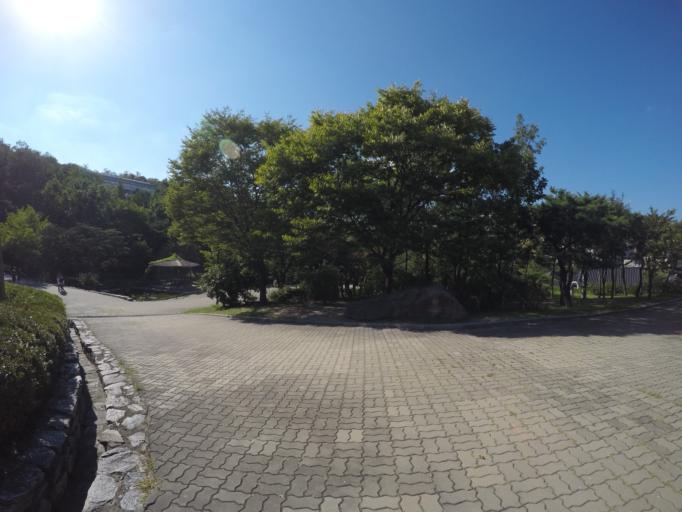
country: KR
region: Seoul
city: Seoul
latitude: 37.5578
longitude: 126.9936
